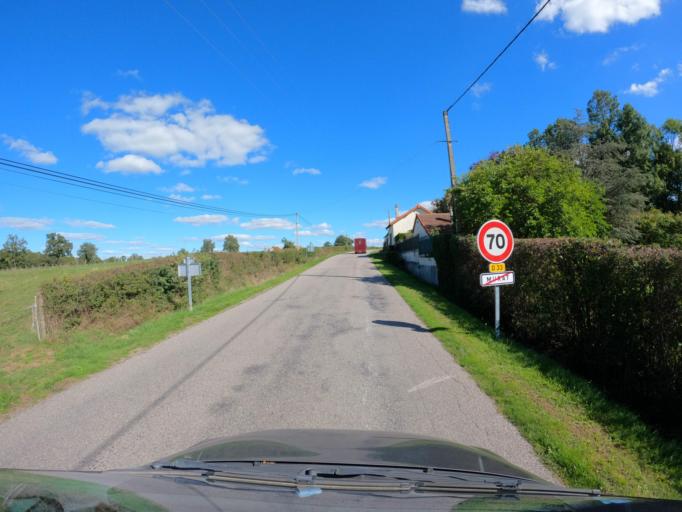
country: FR
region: Auvergne
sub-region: Departement de l'Allier
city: Buxieres-les-Mines
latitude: 46.4053
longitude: 2.9117
